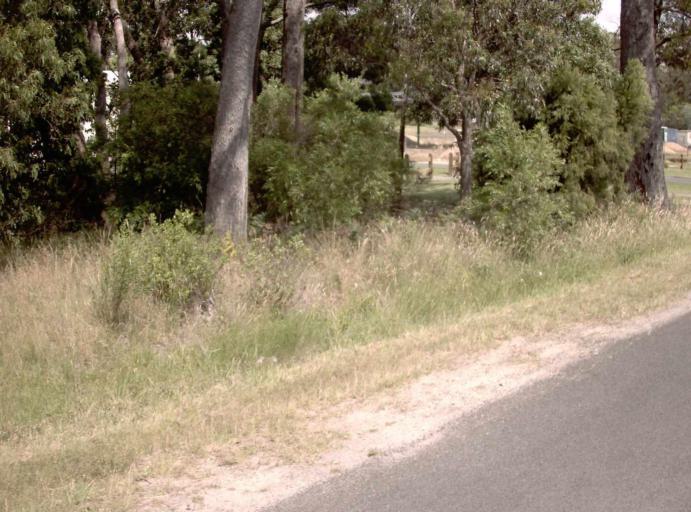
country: AU
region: Victoria
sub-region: Latrobe
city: Traralgon
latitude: -38.2965
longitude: 146.5381
